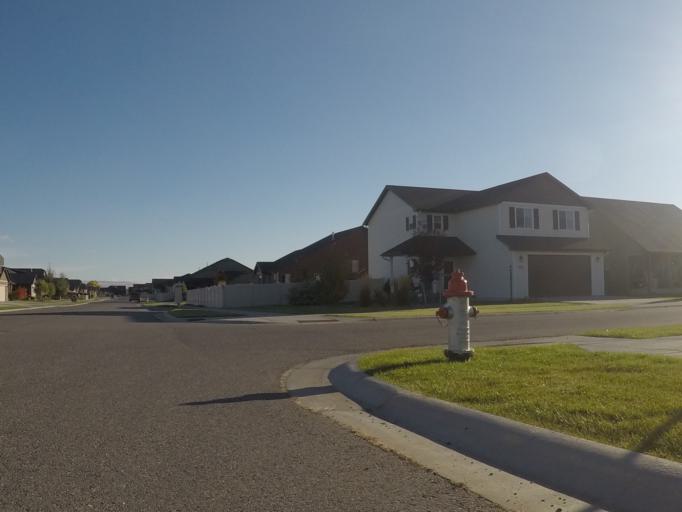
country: US
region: Montana
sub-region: Yellowstone County
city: Laurel
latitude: 45.7836
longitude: -108.6649
